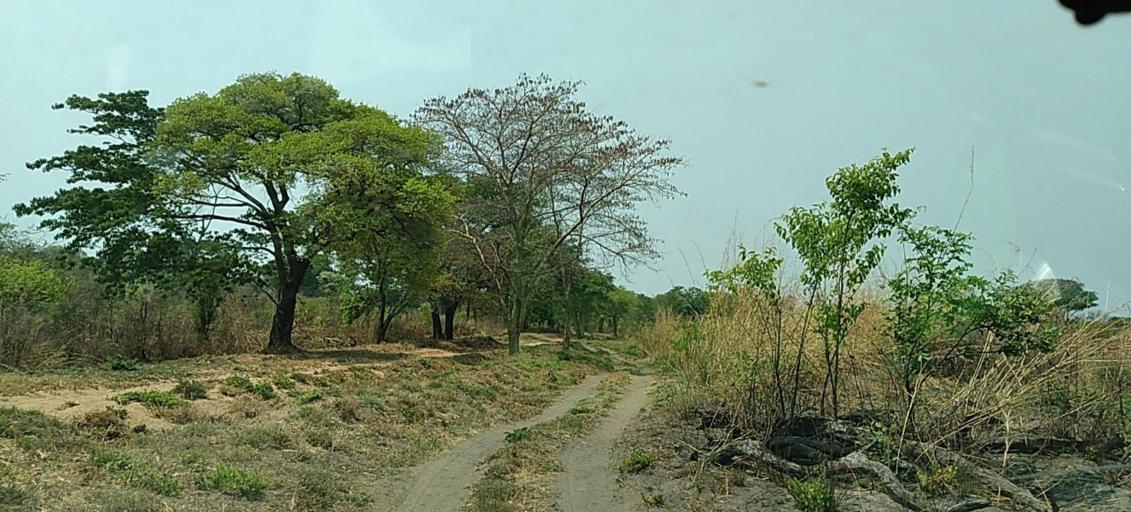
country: ZM
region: Western
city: Lukulu
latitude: -13.9691
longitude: 23.2295
